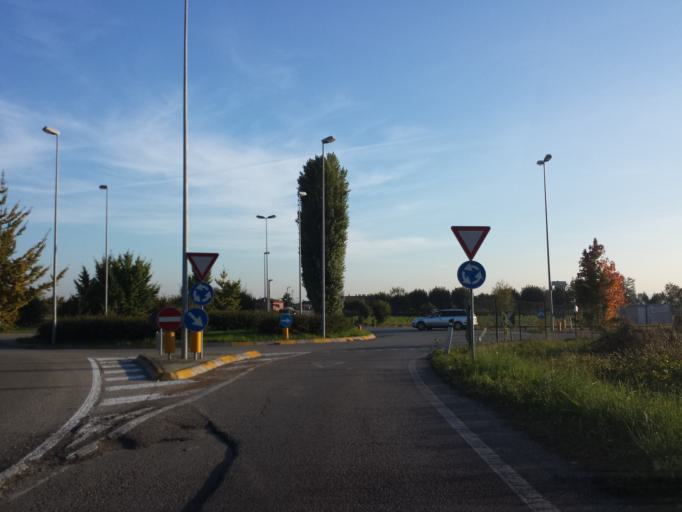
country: IT
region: Veneto
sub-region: Provincia di Vicenza
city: Crispi Cavour
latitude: 45.5838
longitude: 11.5338
